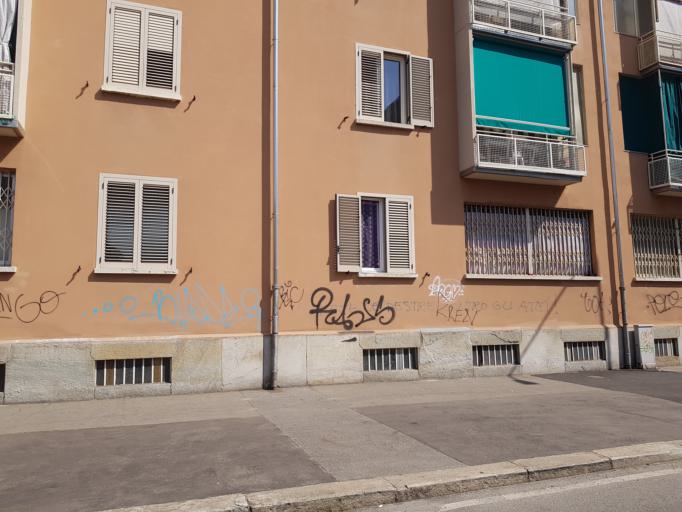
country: IT
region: Piedmont
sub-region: Provincia di Torino
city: Lesna
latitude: 45.0609
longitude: 7.6381
